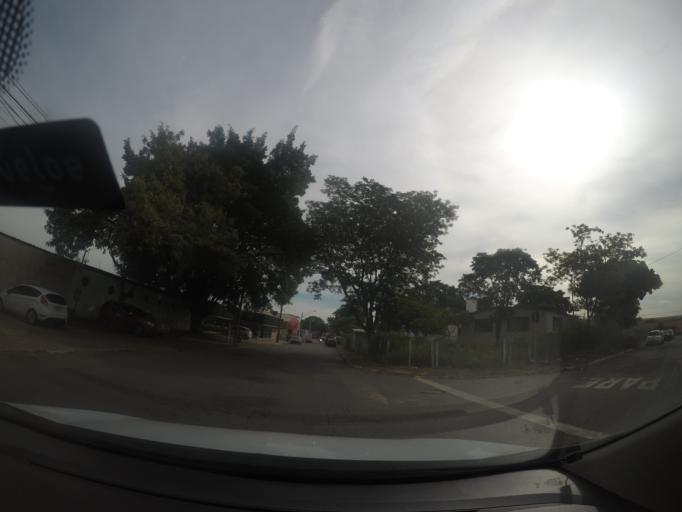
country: BR
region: Goias
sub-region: Goiania
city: Goiania
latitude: -16.6616
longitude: -49.3095
